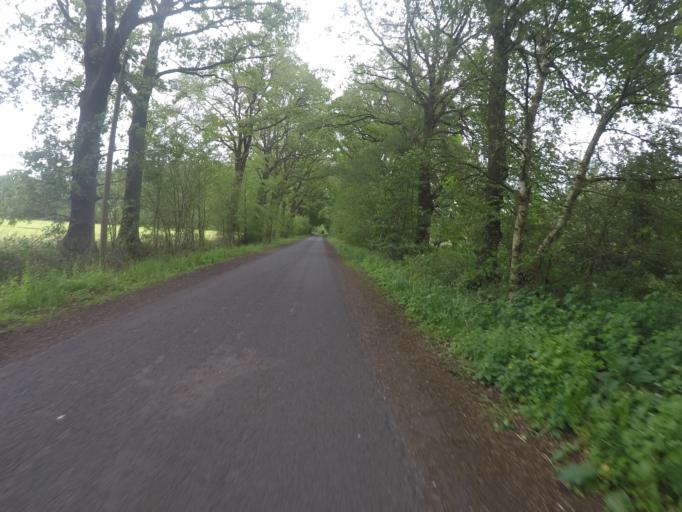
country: DE
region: Schleswig-Holstein
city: Bonningstedt
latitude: 53.6696
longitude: 9.9278
